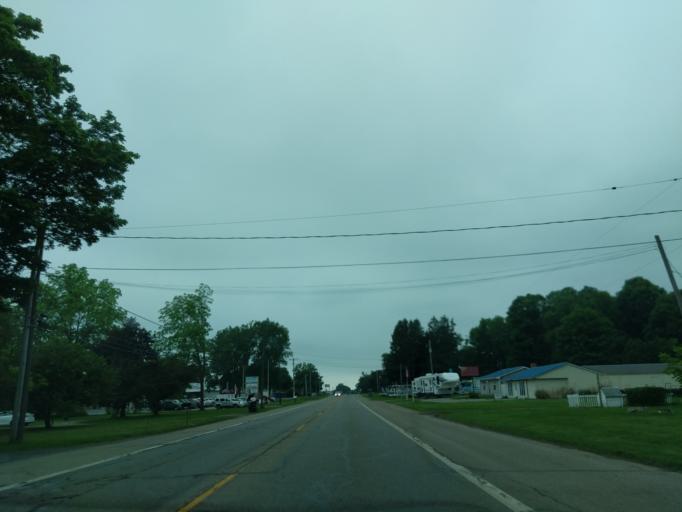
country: US
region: Michigan
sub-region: Branch County
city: Quincy
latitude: 41.9403
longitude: -84.9084
